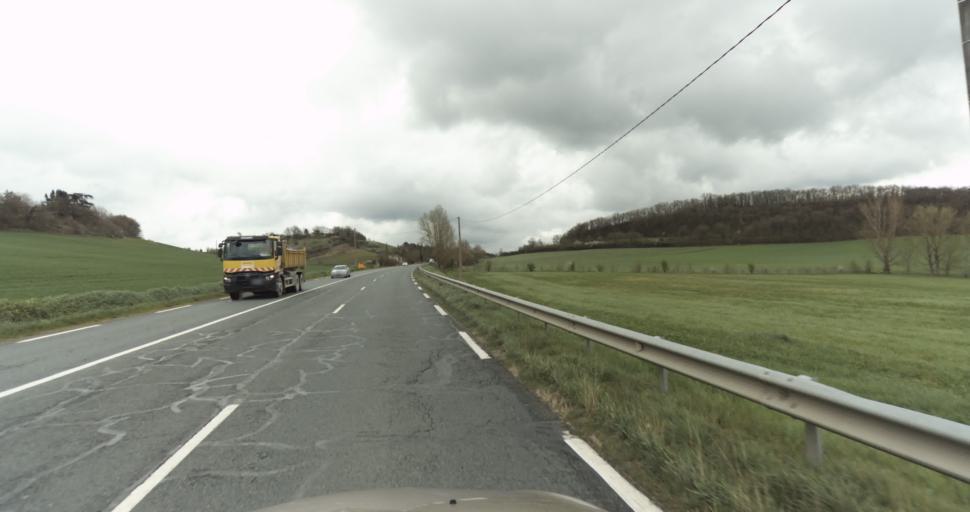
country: FR
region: Midi-Pyrenees
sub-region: Departement du Tarn
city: Puygouzon
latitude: 43.8706
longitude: 2.1828
